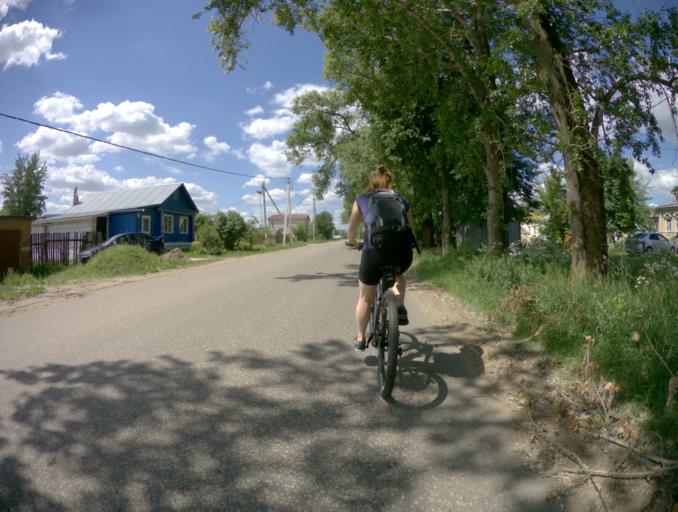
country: RU
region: Vladimir
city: Bogolyubovo
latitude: 56.1909
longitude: 40.4967
